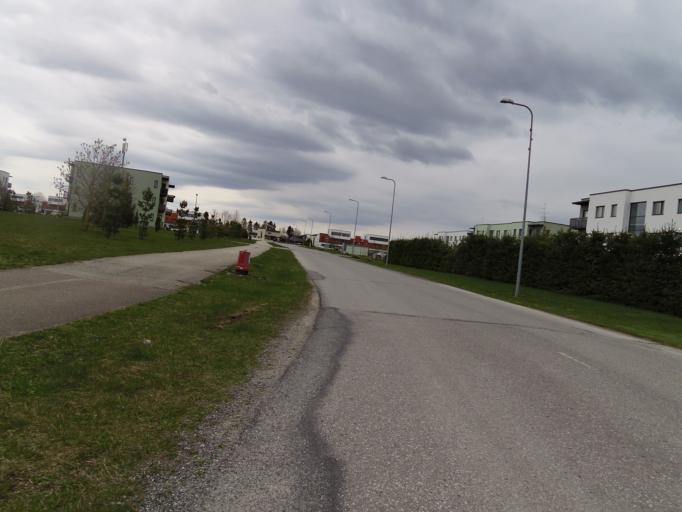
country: EE
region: Harju
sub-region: Tallinna linn
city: Tallinn
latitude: 59.3953
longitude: 24.8035
